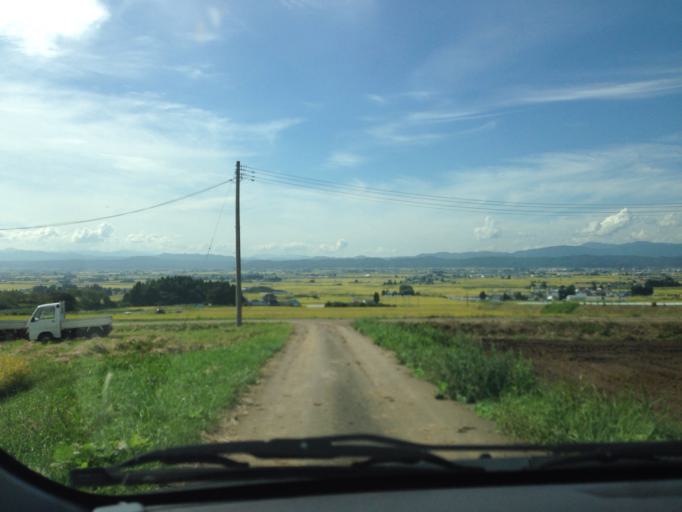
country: JP
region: Fukushima
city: Kitakata
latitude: 37.6186
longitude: 139.9320
